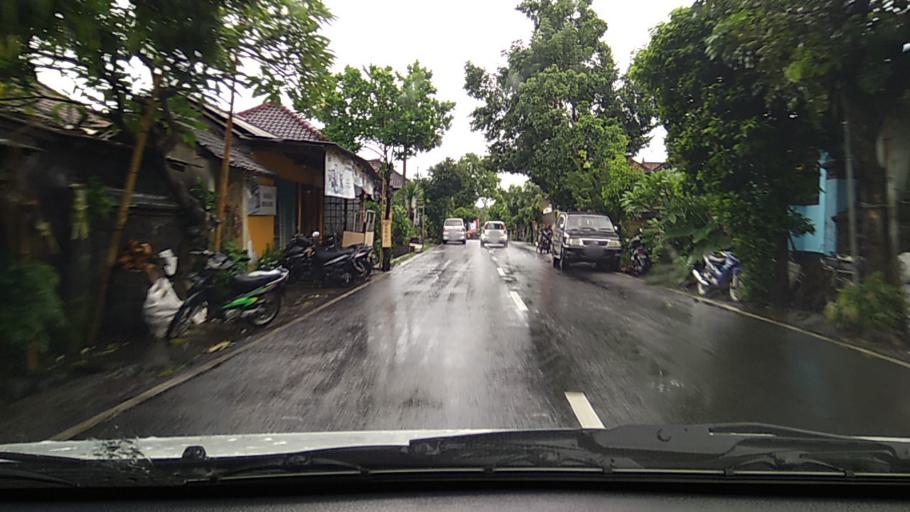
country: ID
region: Bali
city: Banjar Timbrah
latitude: -8.4844
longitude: 115.6038
